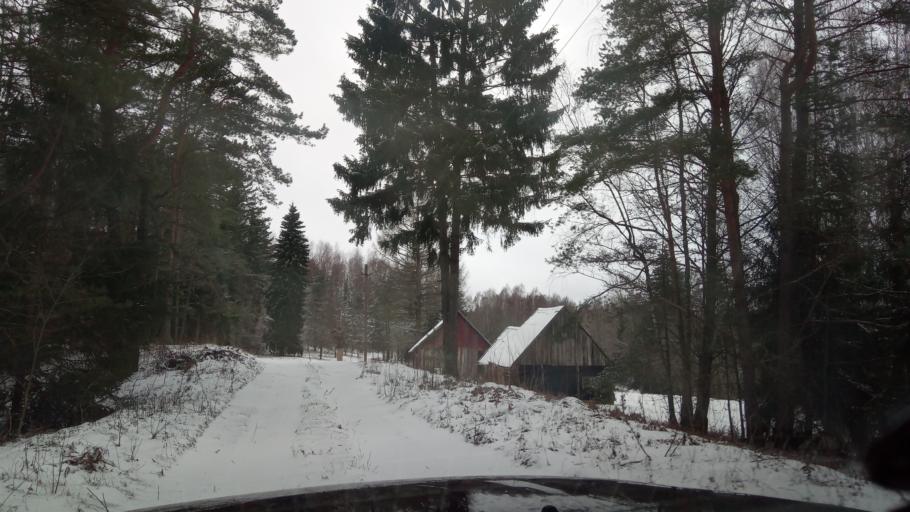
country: LT
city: Zarasai
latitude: 55.6619
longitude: 26.0968
